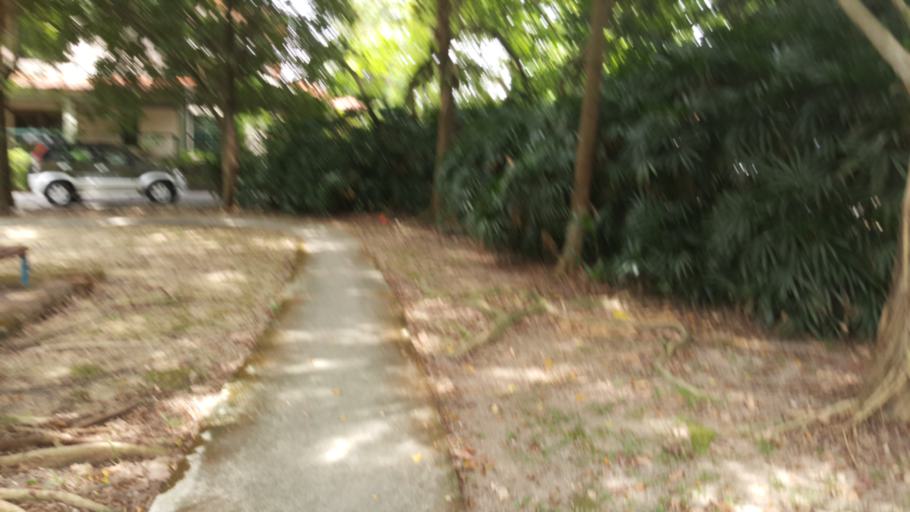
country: MY
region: Selangor
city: Kampung Baru Subang
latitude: 3.1453
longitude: 101.5769
